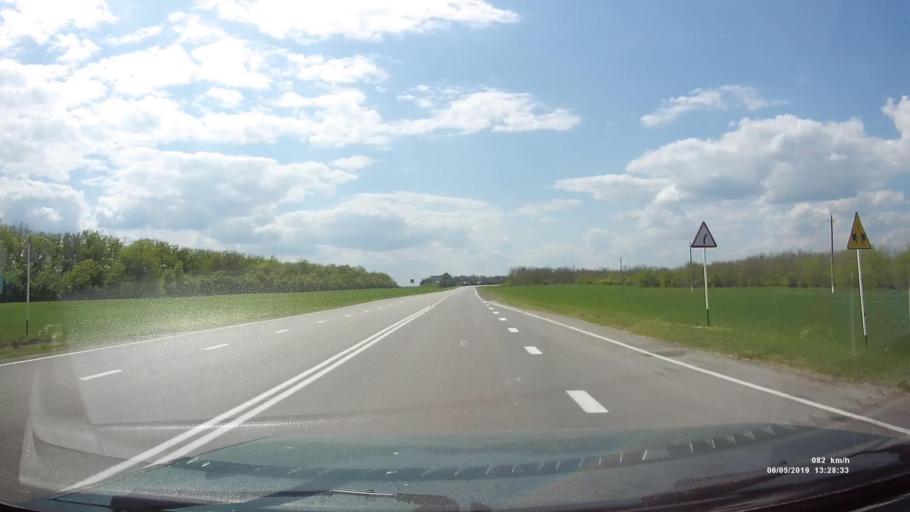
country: RU
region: Rostov
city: Ust'-Donetskiy
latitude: 47.6693
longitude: 40.8605
